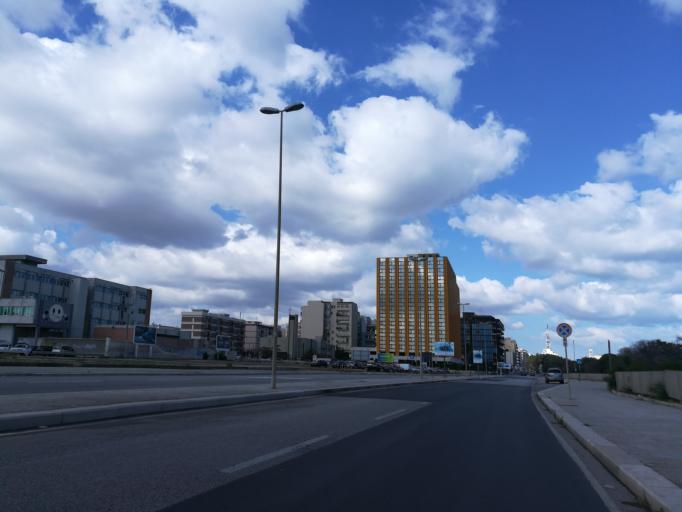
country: IT
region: Apulia
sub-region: Provincia di Bari
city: Bari
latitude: 41.1165
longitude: 16.8968
